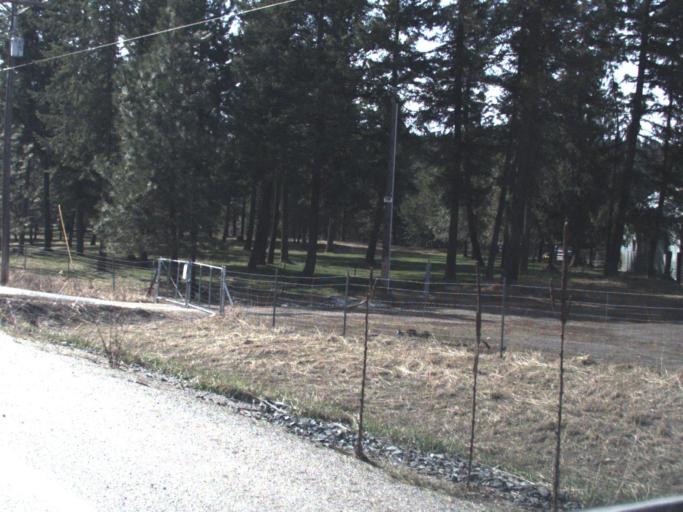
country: US
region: Washington
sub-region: Stevens County
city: Colville
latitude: 48.5259
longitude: -117.8183
